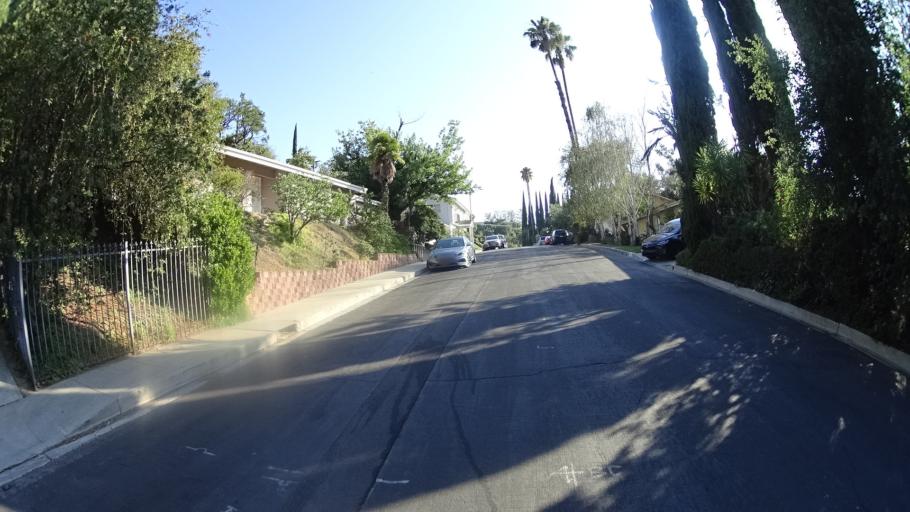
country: US
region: California
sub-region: Los Angeles County
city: Universal City
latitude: 34.1331
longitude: -118.3748
